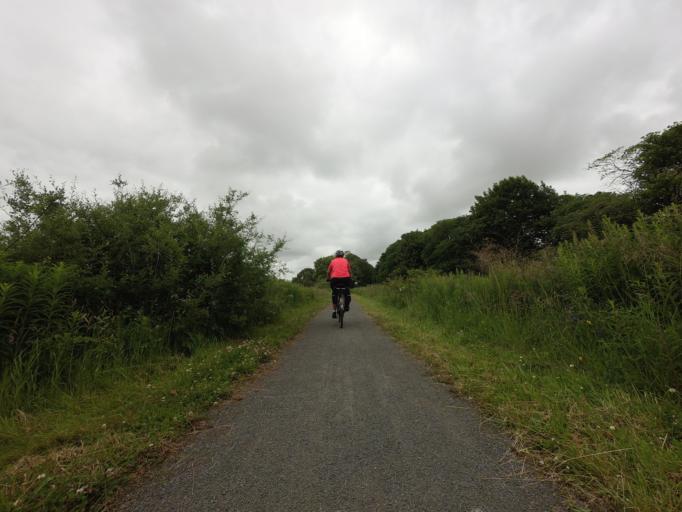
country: GB
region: Scotland
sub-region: Aberdeenshire
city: Ellon
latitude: 57.4776
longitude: -2.1298
